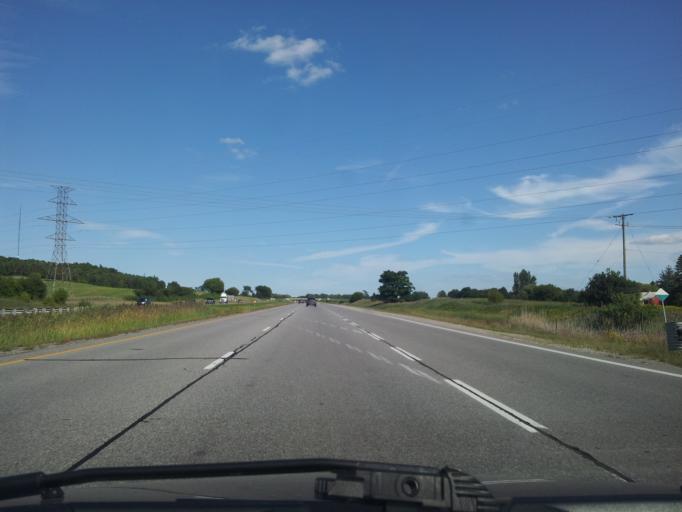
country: CA
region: Ontario
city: Kitchener
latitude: 43.3936
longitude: -80.6551
